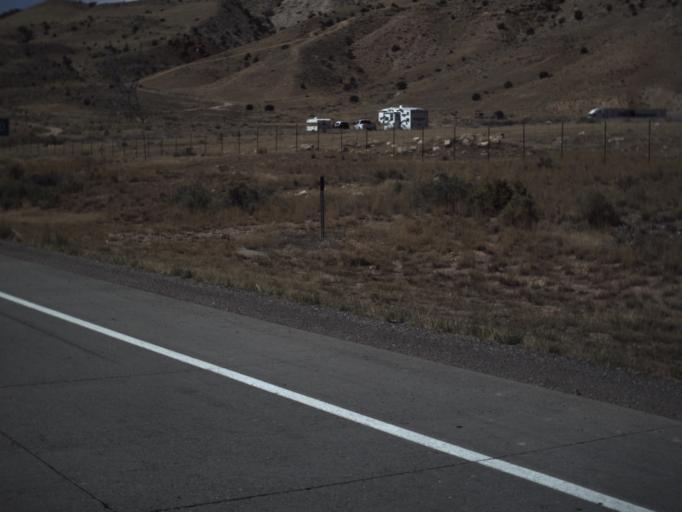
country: US
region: Utah
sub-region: Sevier County
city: Richfield
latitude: 38.7919
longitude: -112.0800
